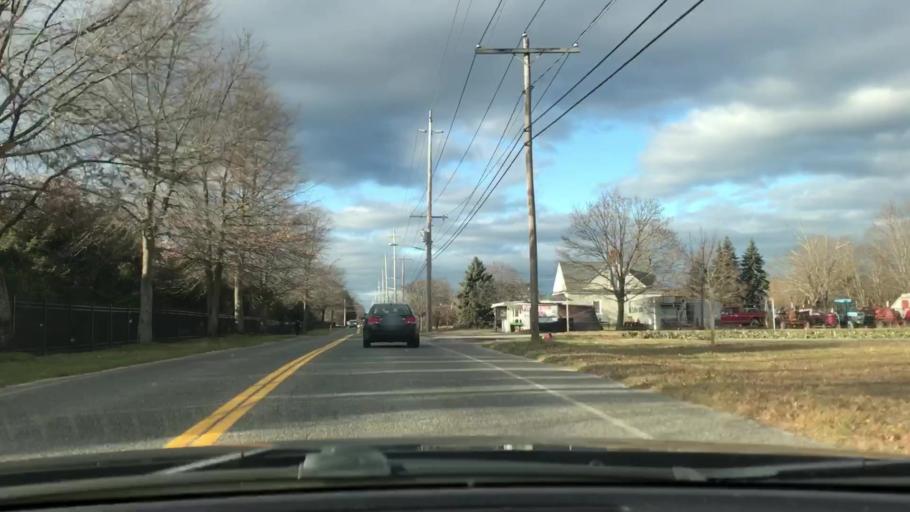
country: US
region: New York
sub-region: Suffolk County
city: Riverhead
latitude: 40.9321
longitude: -72.7030
